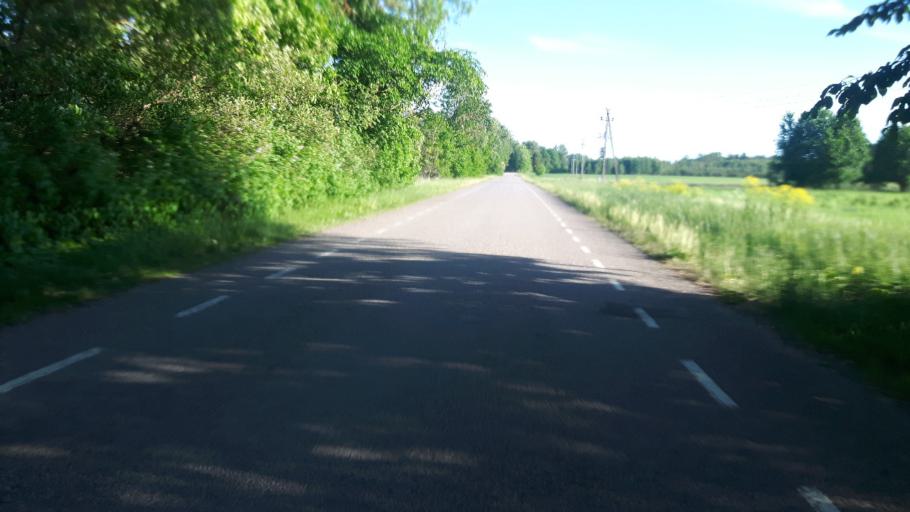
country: EE
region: Raplamaa
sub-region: Kehtna vald
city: Kehtna
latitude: 58.8957
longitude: 24.8798
